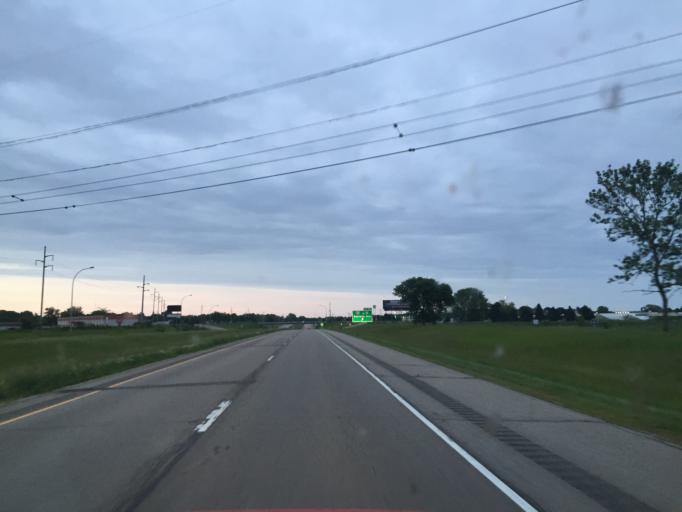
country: US
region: Minnesota
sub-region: Mower County
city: Austin
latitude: 43.6628
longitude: -93.0244
